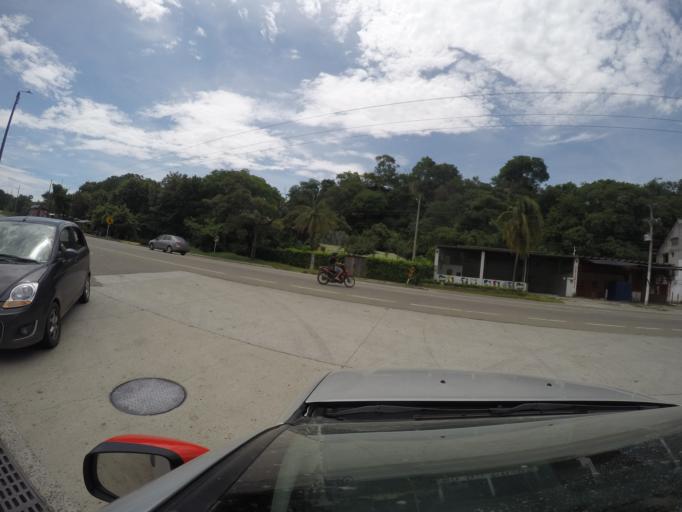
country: CO
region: Tolima
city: Honda
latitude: 5.2142
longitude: -74.7381
